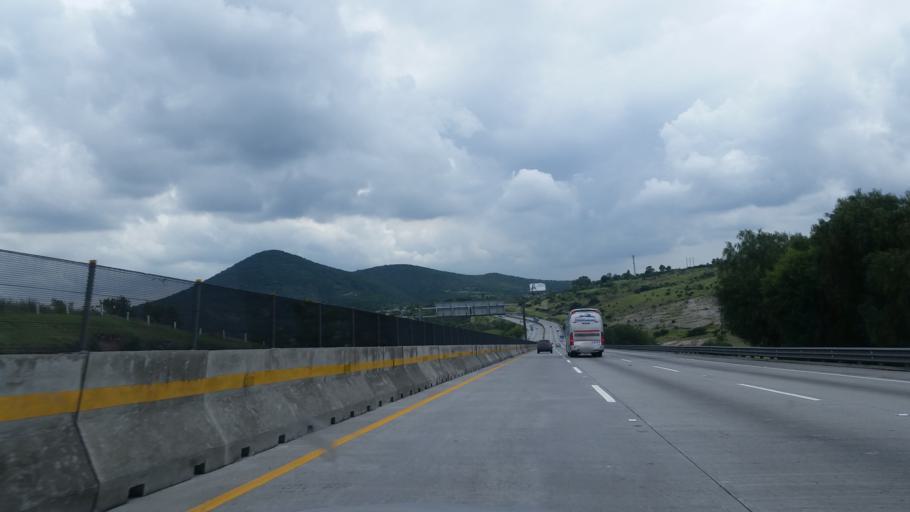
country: MX
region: Hidalgo
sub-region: Tepeji del Rio de Ocampo
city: Santiago Tlautla
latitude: 19.9495
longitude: -99.4005
